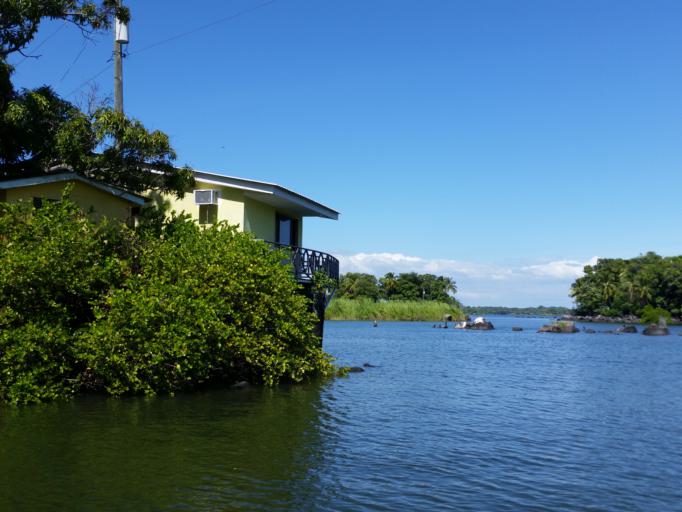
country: NI
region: Granada
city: Granada
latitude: 11.8730
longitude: -85.9035
